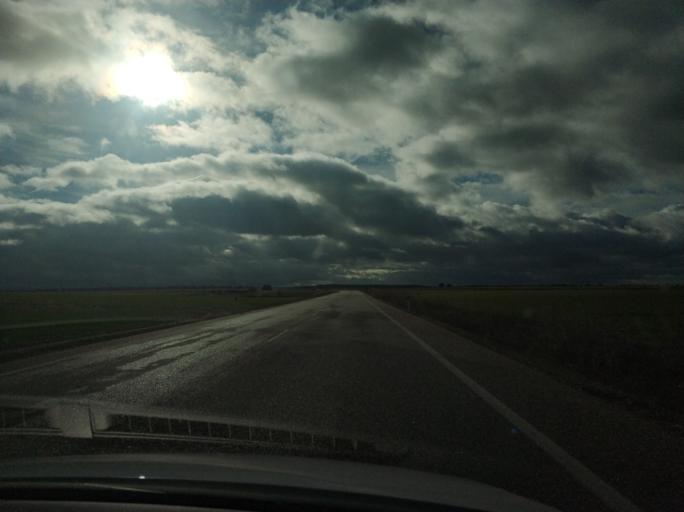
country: ES
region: Castille and Leon
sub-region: Provincia de Segovia
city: Ribota
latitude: 41.4035
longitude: -3.4200
